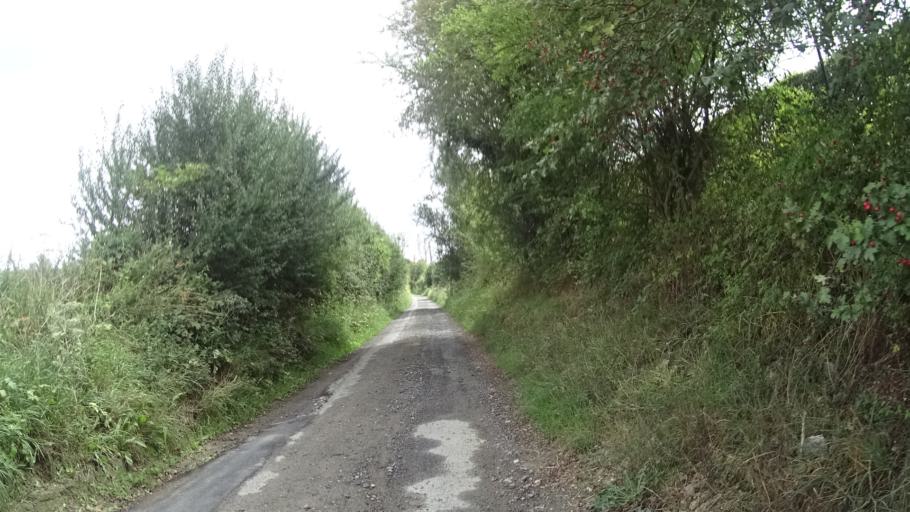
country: FR
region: Nord-Pas-de-Calais
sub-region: Departement du Nord
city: Pont-sur-Sambre
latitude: 50.2123
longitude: 3.8454
